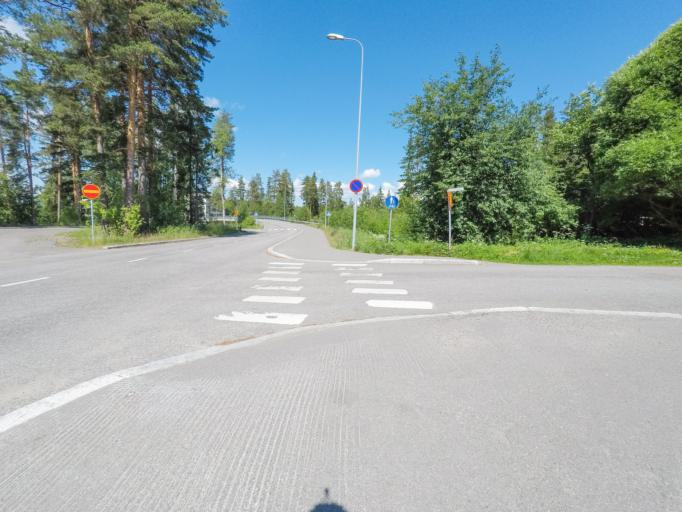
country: FI
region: Southern Savonia
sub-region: Savonlinna
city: Savonlinna
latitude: 61.8788
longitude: 28.8561
